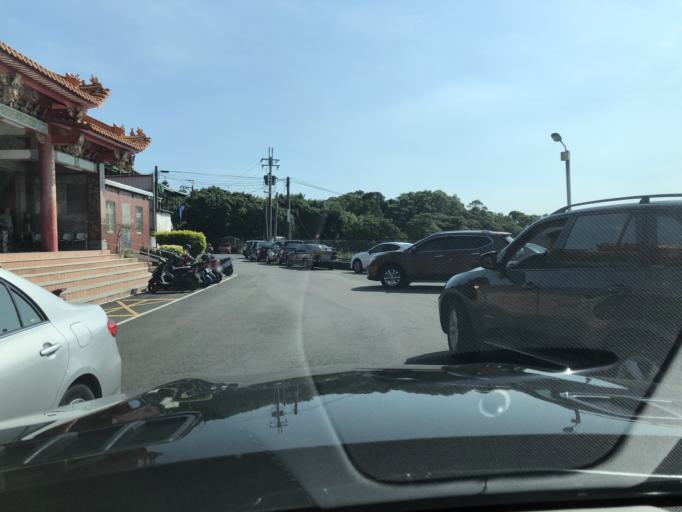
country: TW
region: Taiwan
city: Taoyuan City
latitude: 25.0657
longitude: 121.2936
